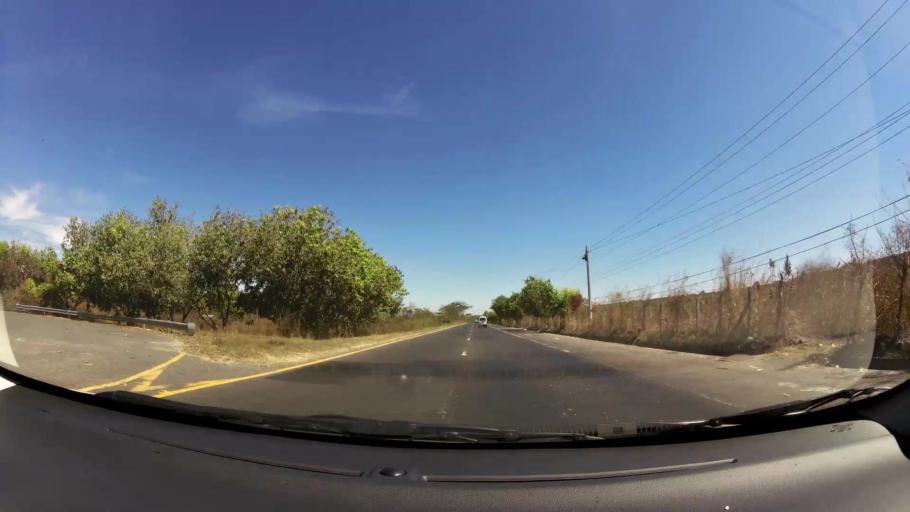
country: SV
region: La Libertad
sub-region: Distrito de Quezaltepeque
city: Quezaltepeque
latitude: 13.8060
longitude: -89.3268
